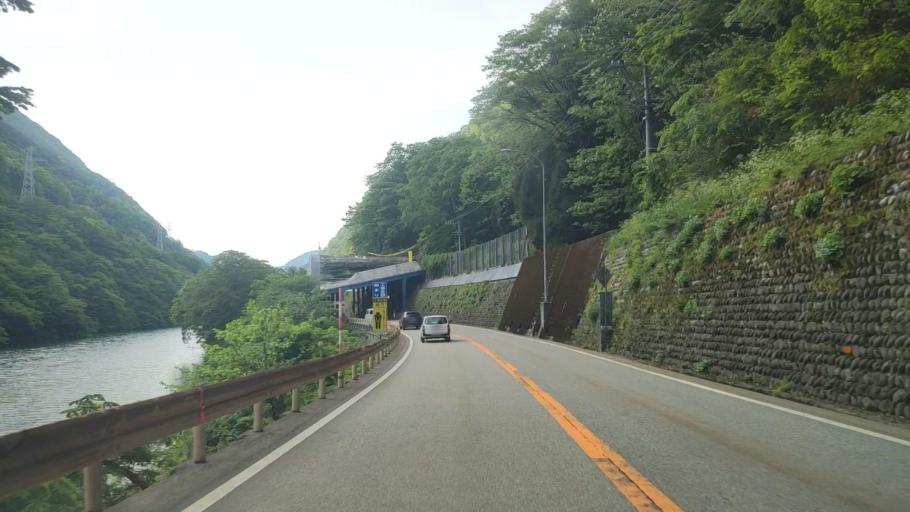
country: JP
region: Toyama
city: Yatsuomachi-higashikumisaka
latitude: 36.4121
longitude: 137.2921
